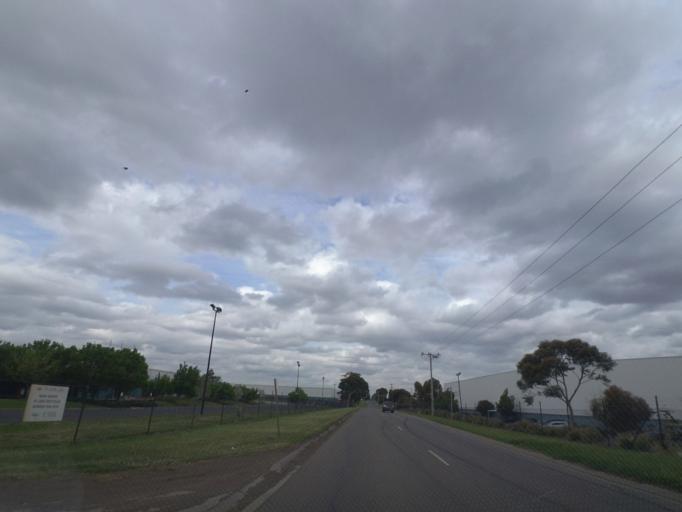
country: AU
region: Victoria
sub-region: Brimbank
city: Keilor Park
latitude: -37.7007
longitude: 144.8488
